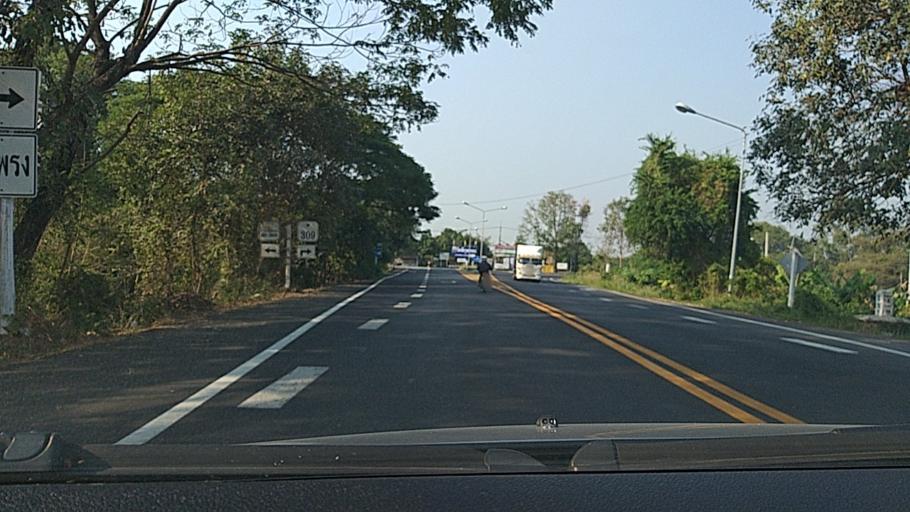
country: TH
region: Sing Buri
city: Phrom Buri
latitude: 14.7585
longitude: 100.4350
